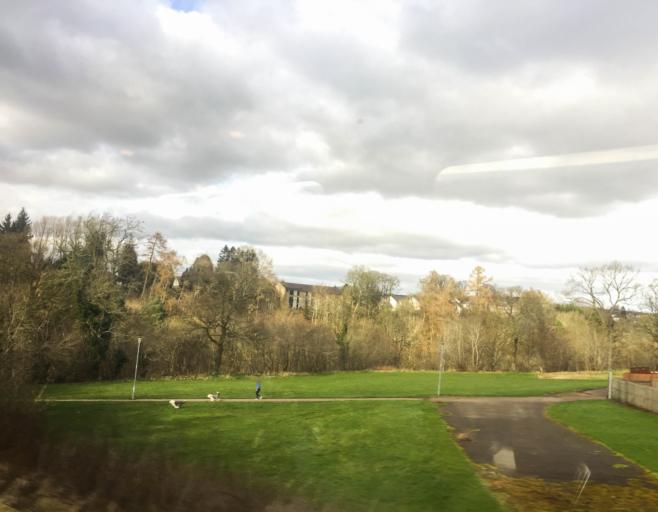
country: GB
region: Scotland
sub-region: South Lanarkshire
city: Carluke
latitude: 55.7296
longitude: -3.8464
